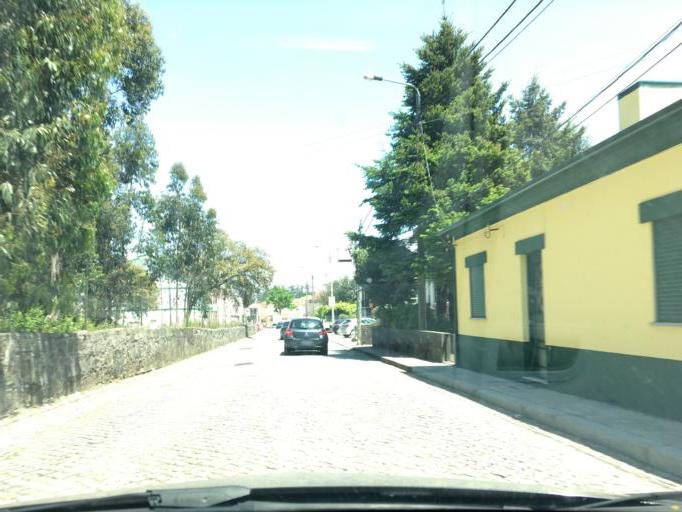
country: PT
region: Porto
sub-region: Maia
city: Anta
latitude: 41.2628
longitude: -8.6351
